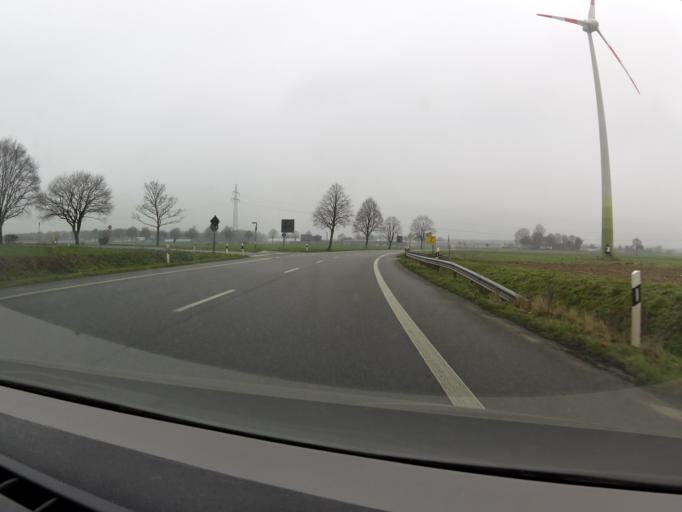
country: DE
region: North Rhine-Westphalia
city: Straelen
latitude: 51.4002
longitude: 6.2608
